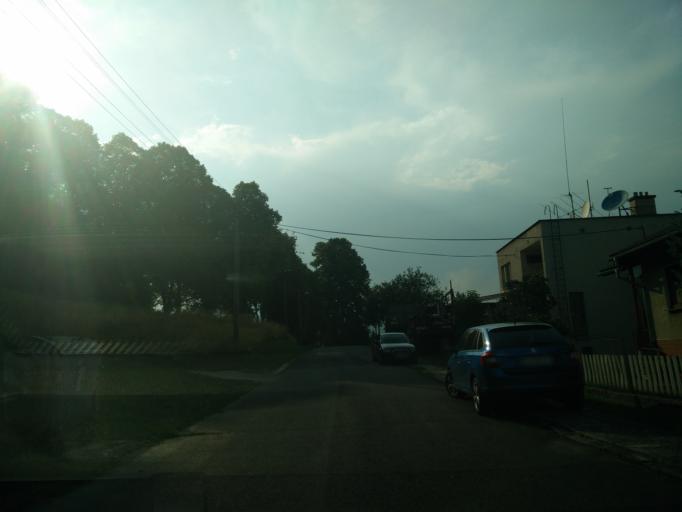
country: SK
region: Banskobystricky
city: Ziar nad Hronom
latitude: 48.5368
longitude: 18.7833
